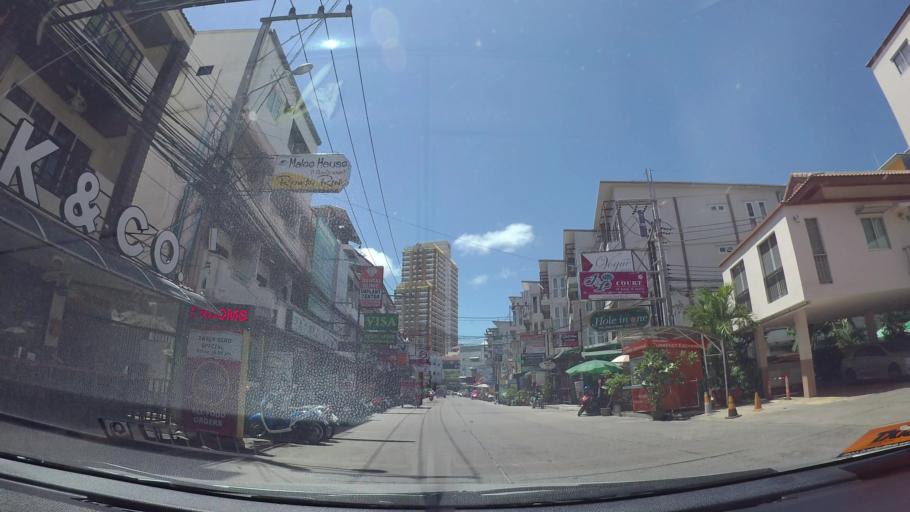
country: TH
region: Chon Buri
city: Phatthaya
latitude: 12.9282
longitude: 100.8857
